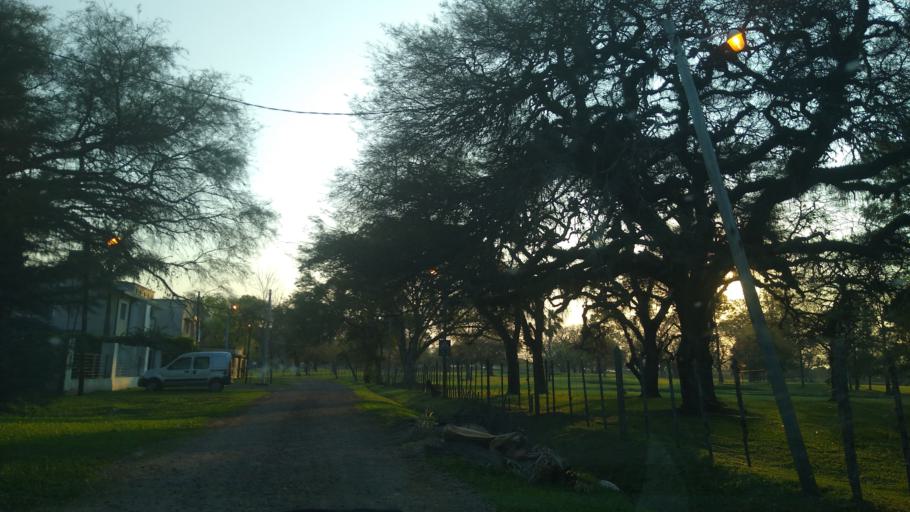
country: AR
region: Chaco
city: Barranqueras
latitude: -27.4690
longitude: -58.9535
